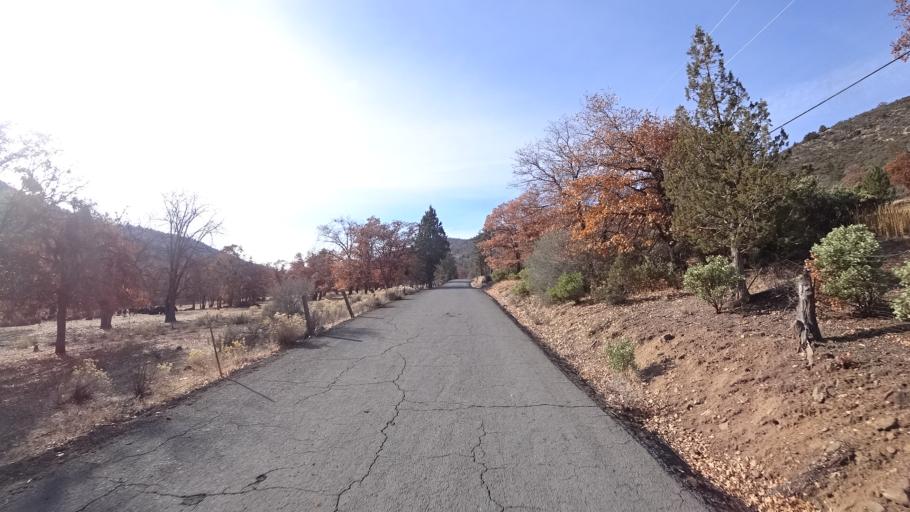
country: US
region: California
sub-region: Siskiyou County
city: Montague
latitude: 41.6230
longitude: -122.5752
